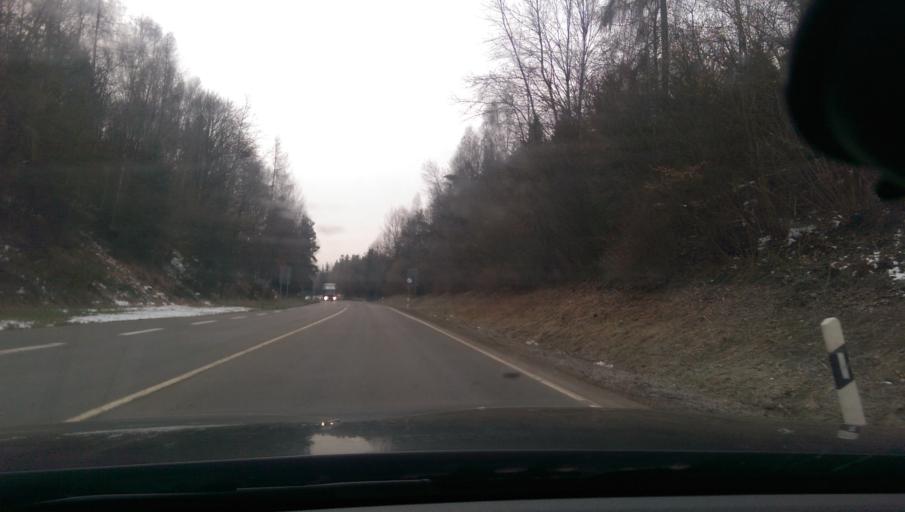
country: DE
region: Bavaria
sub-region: Lower Bavaria
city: Tiefenbach
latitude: 48.6059
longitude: 13.4094
